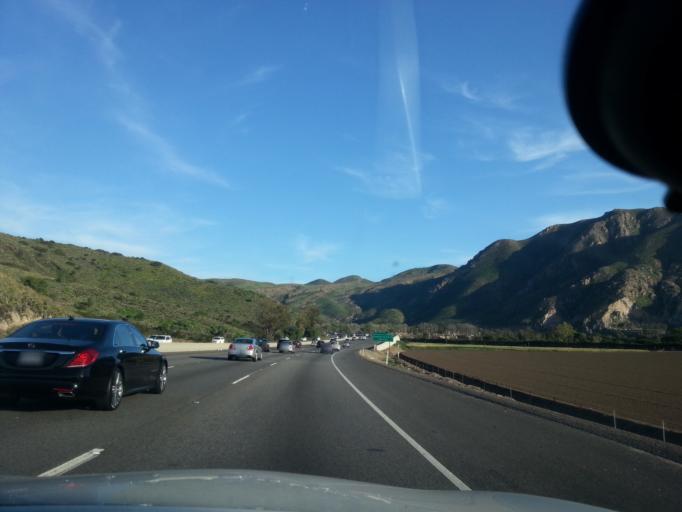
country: US
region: California
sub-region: Ventura County
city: Camarillo
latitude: 34.2088
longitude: -118.9938
